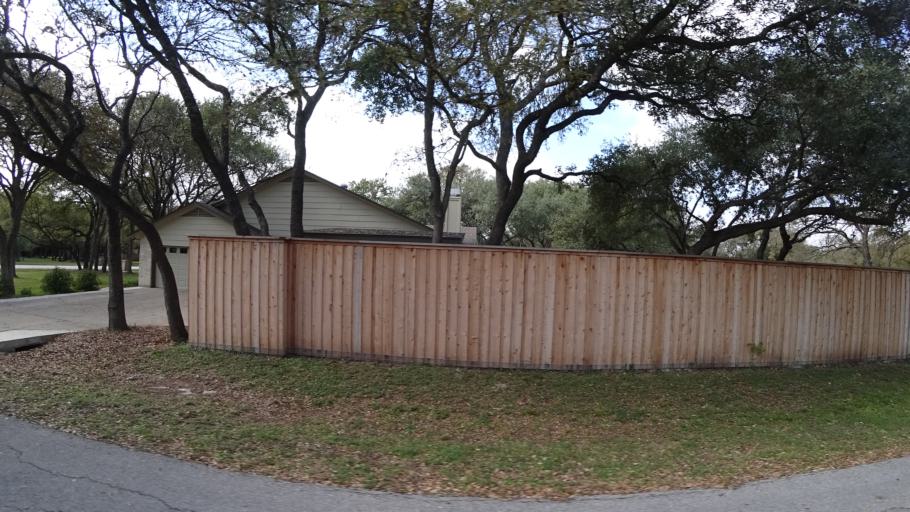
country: US
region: Texas
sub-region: Travis County
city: Shady Hollow
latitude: 30.1602
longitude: -97.8554
